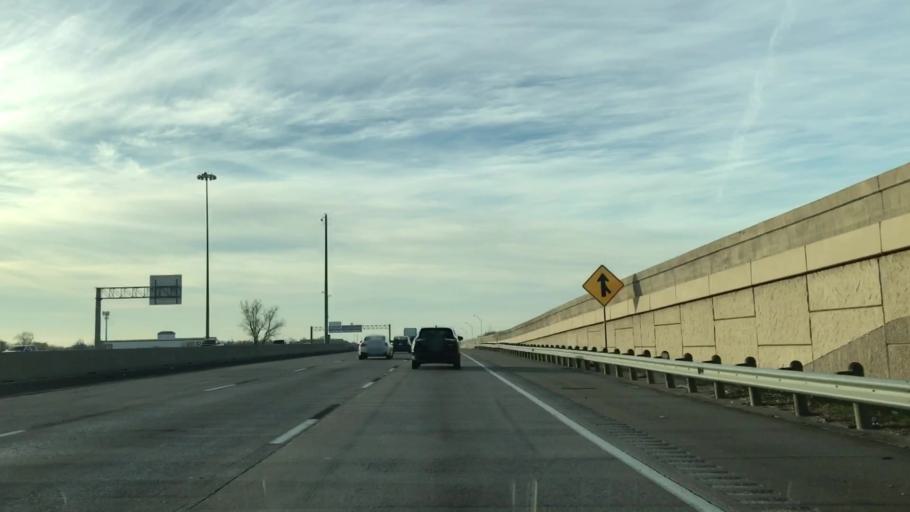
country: US
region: Texas
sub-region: Tarrant County
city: Grapevine
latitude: 32.9043
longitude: -97.0993
